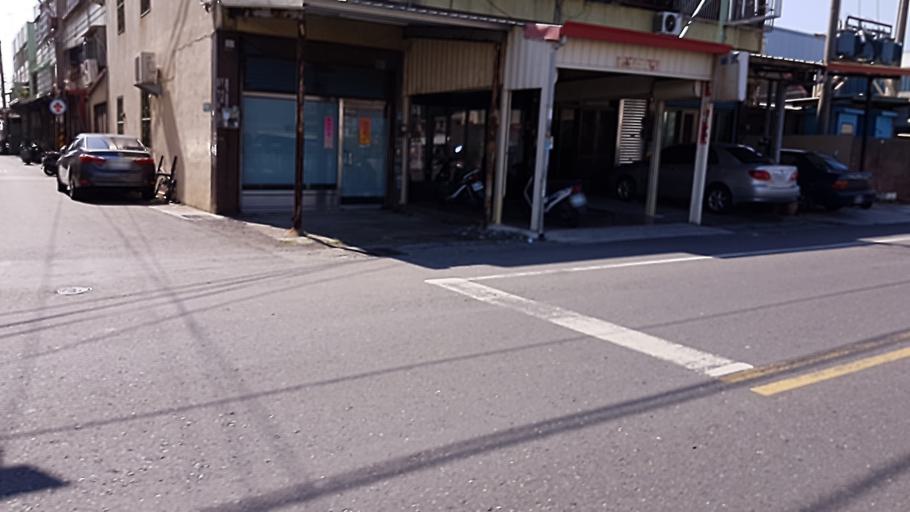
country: TW
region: Taiwan
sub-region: Changhua
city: Chang-hua
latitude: 24.0820
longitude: 120.4913
